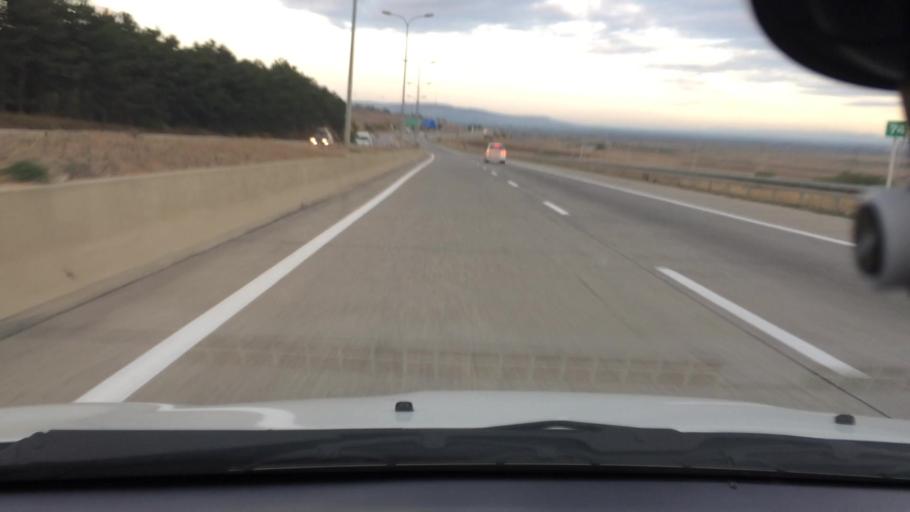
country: GE
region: Shida Kartli
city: Gori
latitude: 42.0274
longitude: 44.2051
